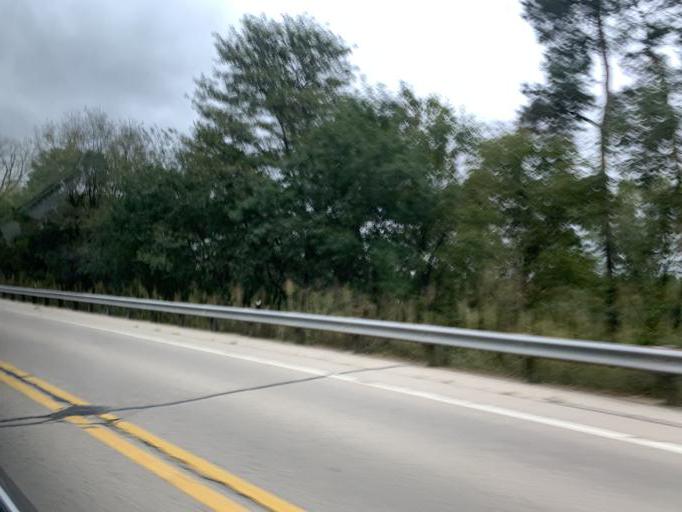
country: US
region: Wisconsin
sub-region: Grant County
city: Muscoda
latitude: 43.2055
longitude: -90.5773
